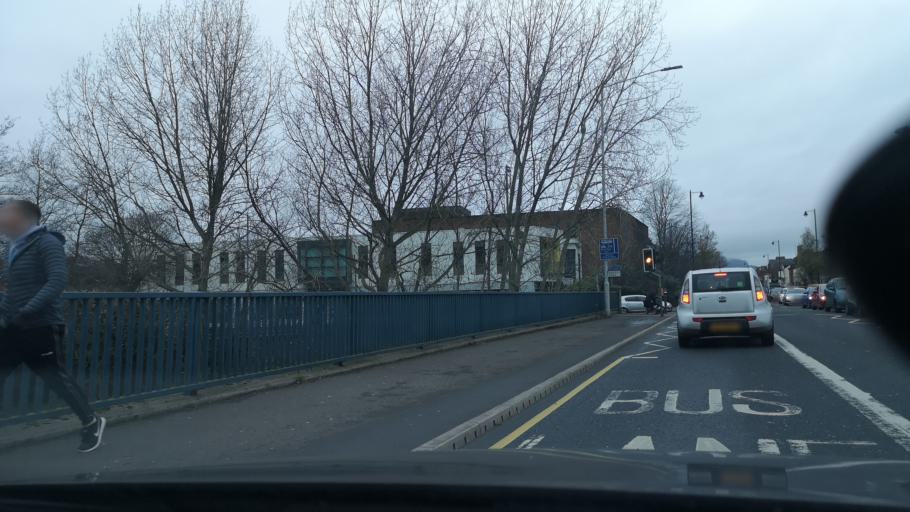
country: GB
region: Northern Ireland
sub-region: City of Belfast
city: Belfast
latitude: 54.5829
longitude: -5.9220
